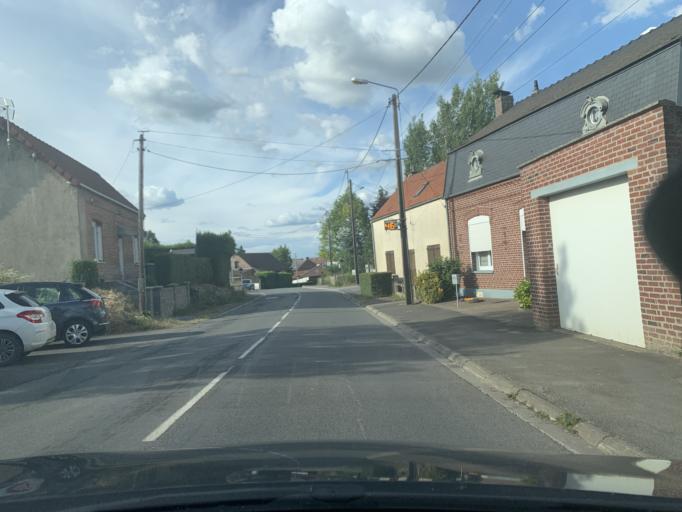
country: FR
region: Nord-Pas-de-Calais
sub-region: Departement du Nord
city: Marcoing
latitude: 50.1166
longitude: 3.1702
